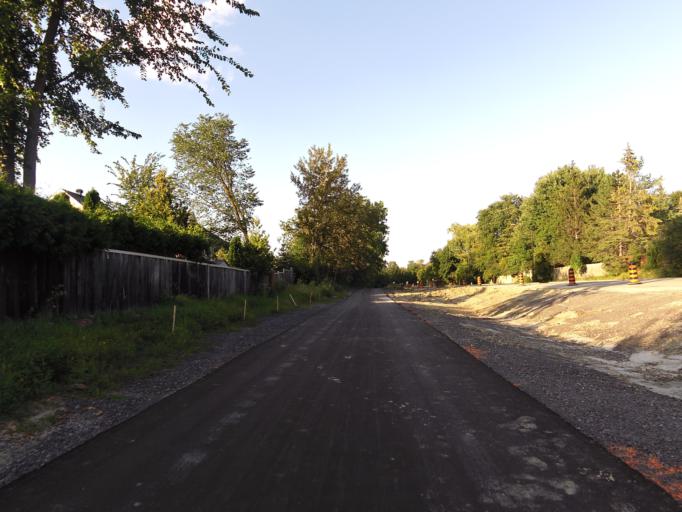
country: CA
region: Ontario
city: Bells Corners
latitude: 45.3133
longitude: -75.8931
